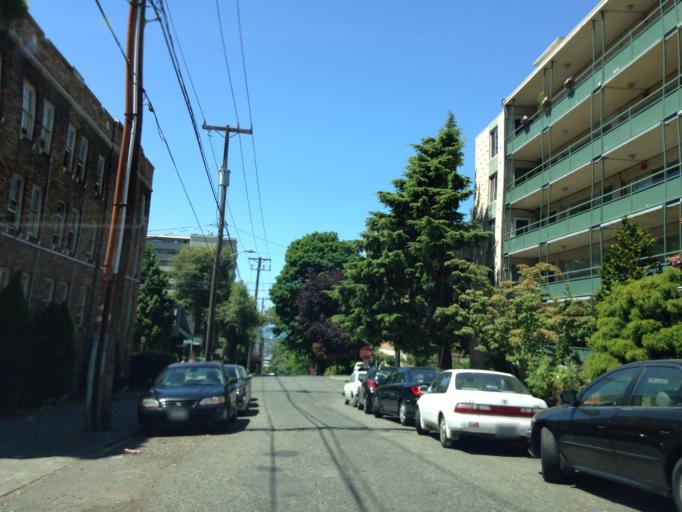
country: US
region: Washington
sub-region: King County
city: Seattle
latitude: 47.6243
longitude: -122.3224
